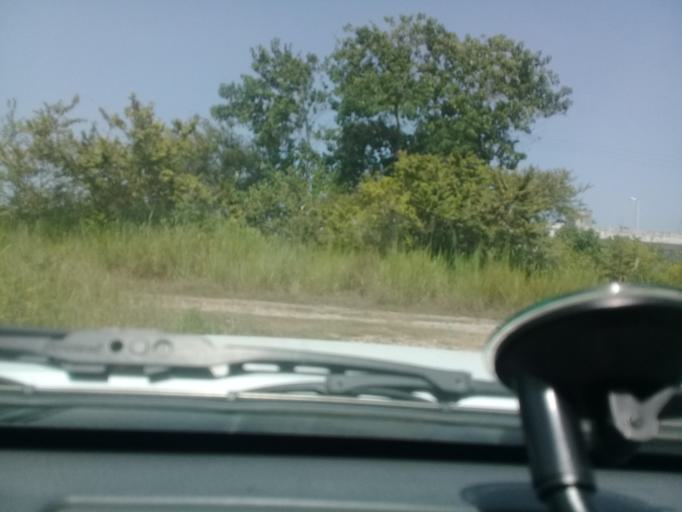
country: MX
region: Veracruz
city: Anahuac
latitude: 22.2178
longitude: -97.8256
